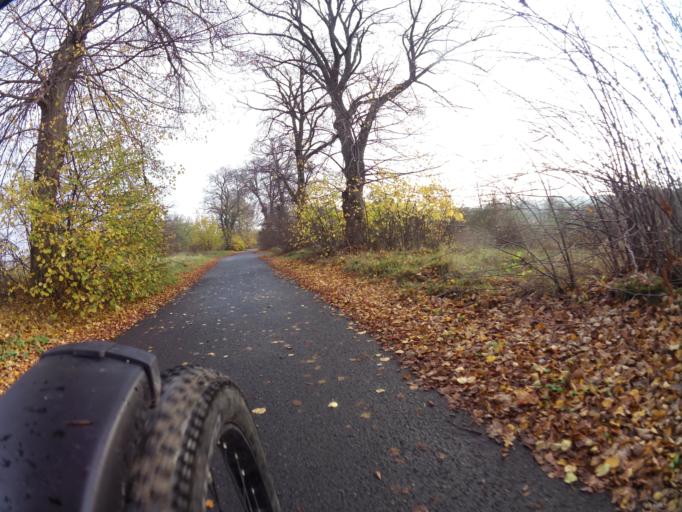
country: PL
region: Pomeranian Voivodeship
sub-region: Powiat wejherowski
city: Gniewino
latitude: 54.7122
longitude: 18.0964
